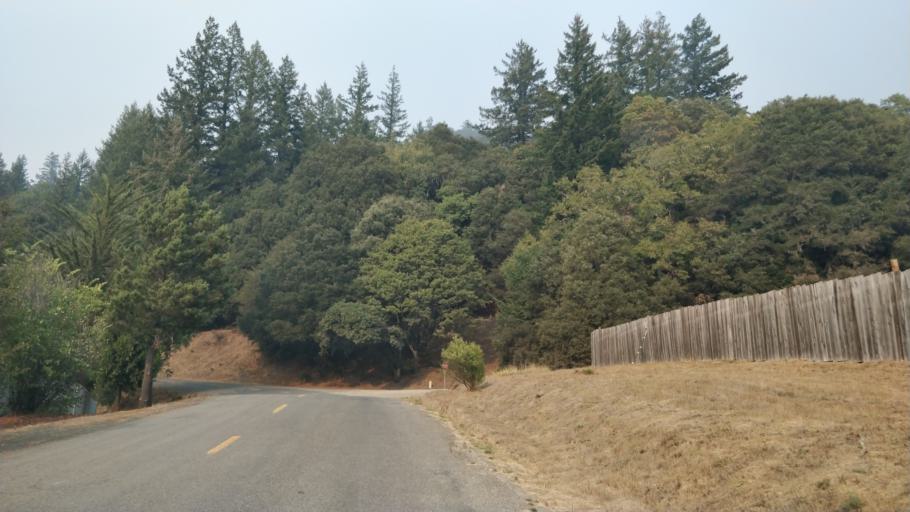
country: US
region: California
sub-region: Humboldt County
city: Rio Dell
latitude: 40.2465
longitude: -124.1224
